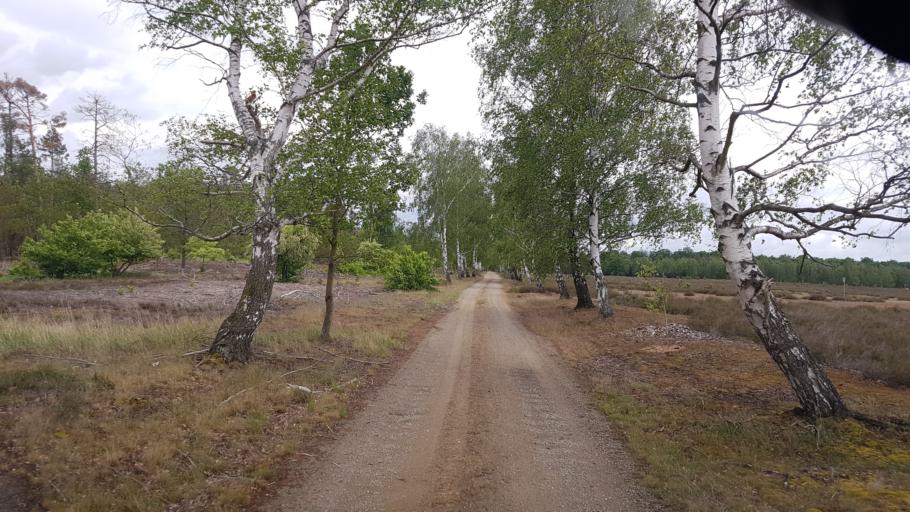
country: DE
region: Brandenburg
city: Hohenleipisch
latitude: 51.5351
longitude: 13.5380
